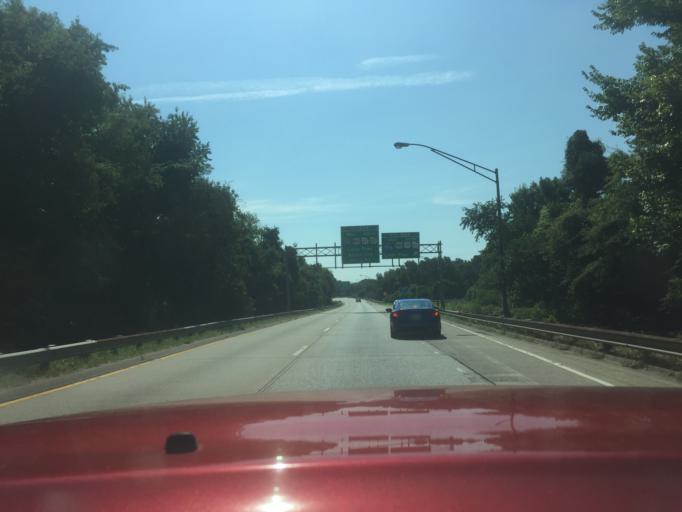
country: US
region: Georgia
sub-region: Chatham County
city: Savannah
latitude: 32.0715
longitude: -81.1388
